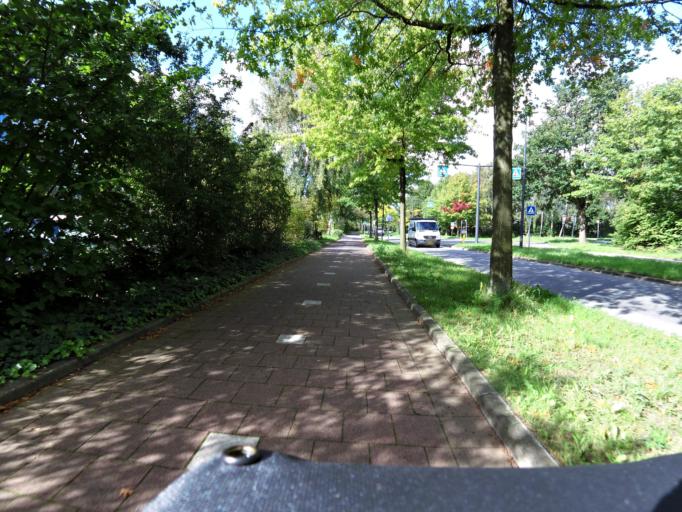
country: NL
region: South Holland
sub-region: Gemeente Vlaardingen
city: Vlaardingen
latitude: 51.9347
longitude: 4.3352
